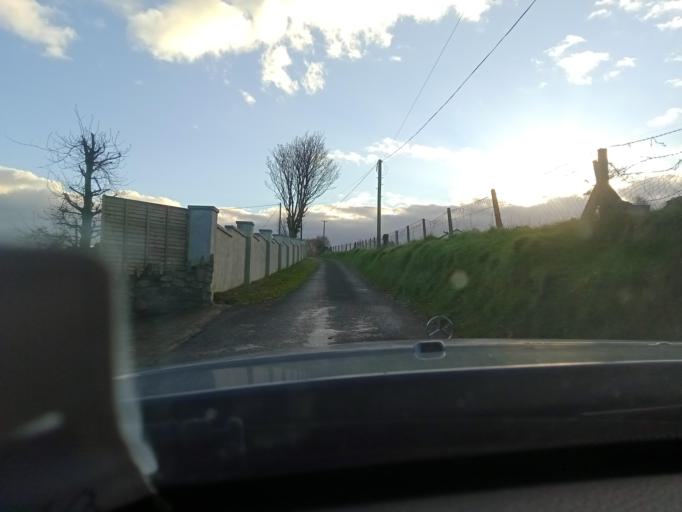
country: IE
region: Leinster
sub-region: Kilkenny
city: Graiguenamanagh
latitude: 52.5001
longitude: -6.9439
